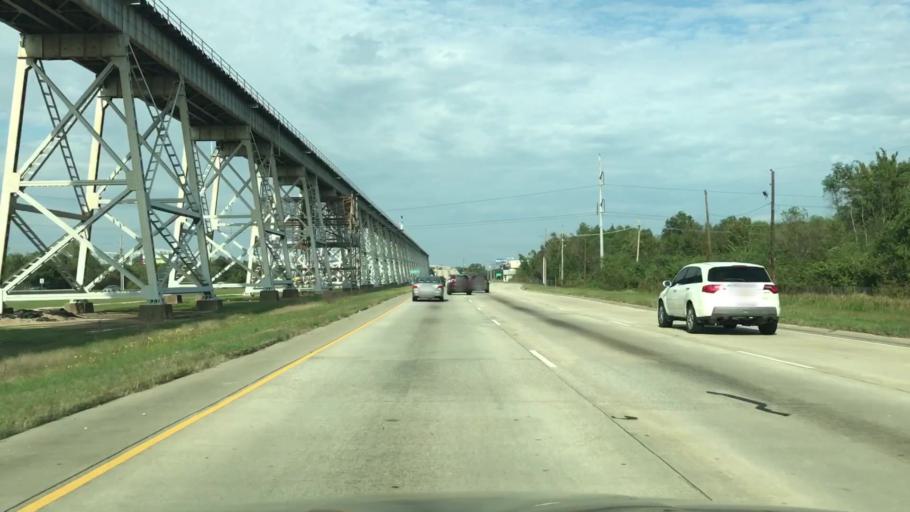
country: US
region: Louisiana
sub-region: Jefferson Parish
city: Bridge City
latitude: 29.9248
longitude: -90.1673
